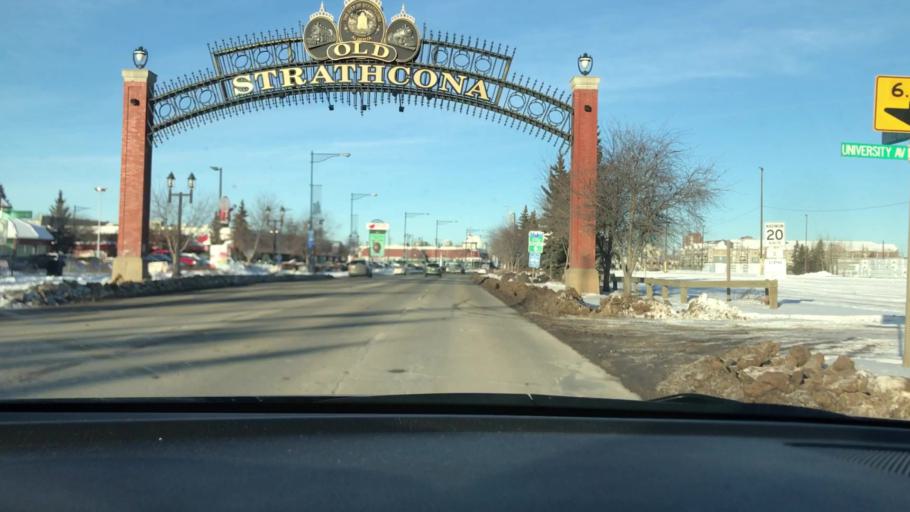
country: CA
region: Alberta
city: Edmonton
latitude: 53.5112
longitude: -113.4943
